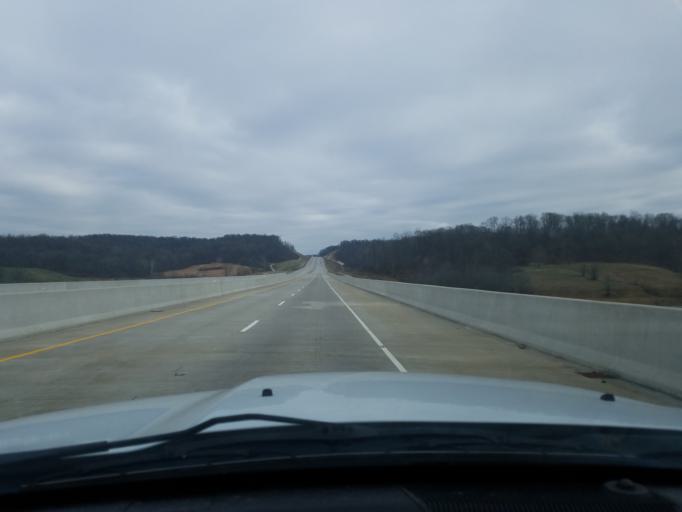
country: US
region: Indiana
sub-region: Greene County
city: Bloomfield
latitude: 38.9612
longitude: -86.8341
